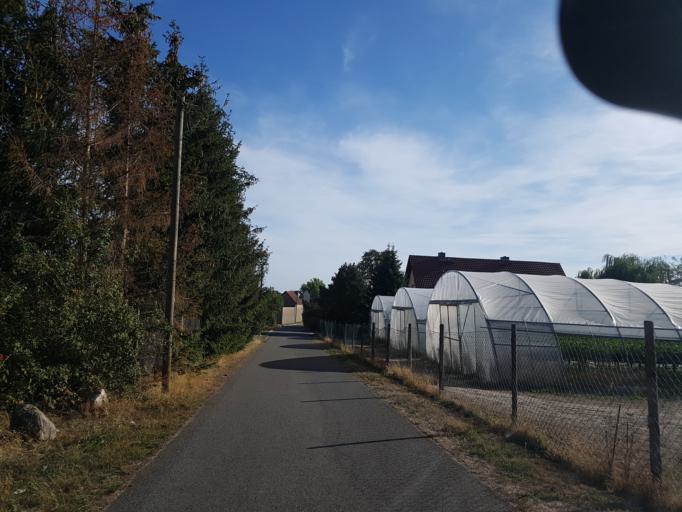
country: DE
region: Saxony-Anhalt
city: Jessen
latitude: 51.7982
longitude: 12.9942
